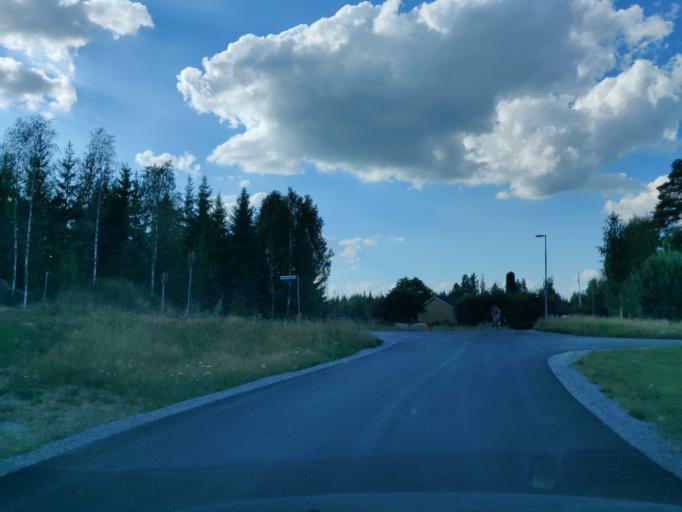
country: SE
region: Vaermland
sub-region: Hagfors Kommun
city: Hagfors
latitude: 60.0188
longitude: 13.6774
